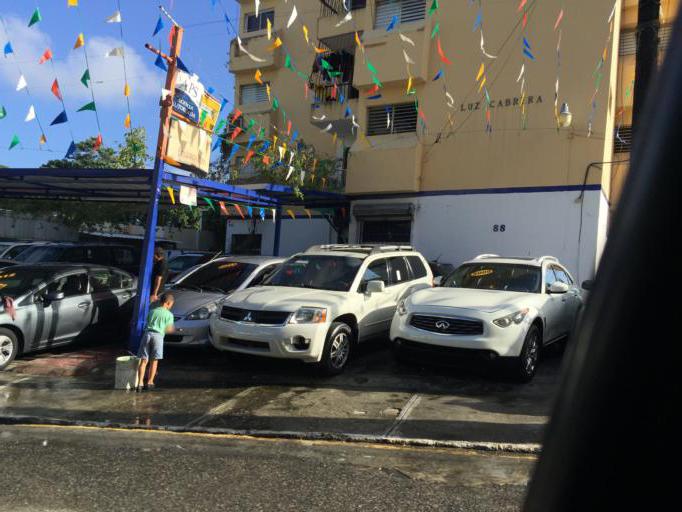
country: DO
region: Nacional
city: La Julia
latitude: 18.4607
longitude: -69.9234
